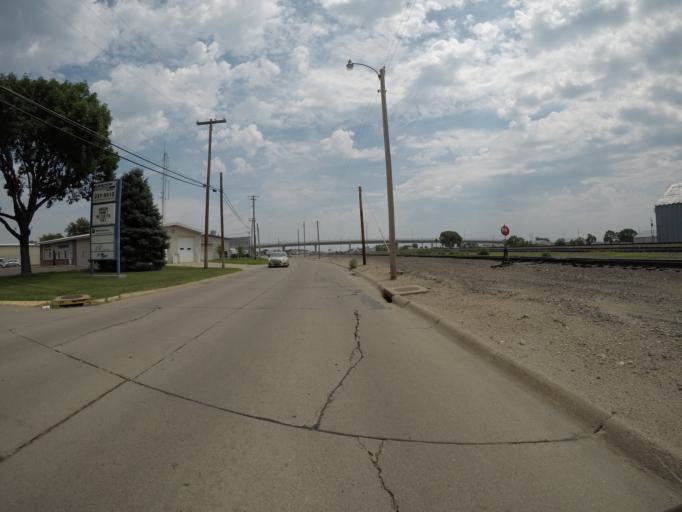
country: US
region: Nebraska
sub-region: Buffalo County
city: Kearney
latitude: 40.6980
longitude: -99.0695
